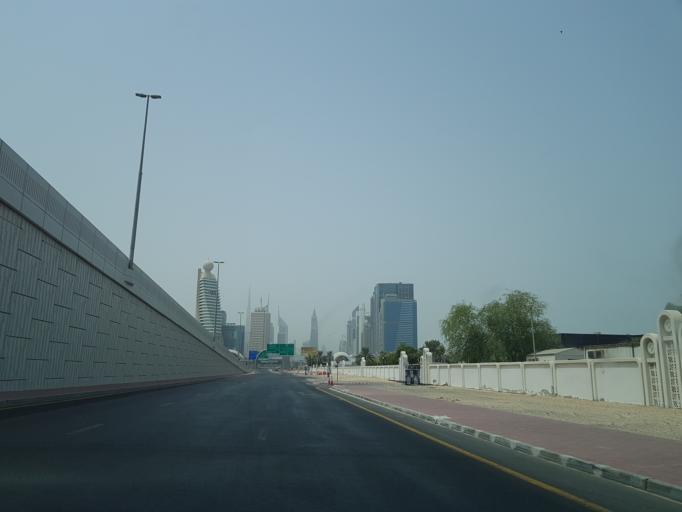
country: AE
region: Ash Shariqah
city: Sharjah
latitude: 25.2386
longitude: 55.2945
